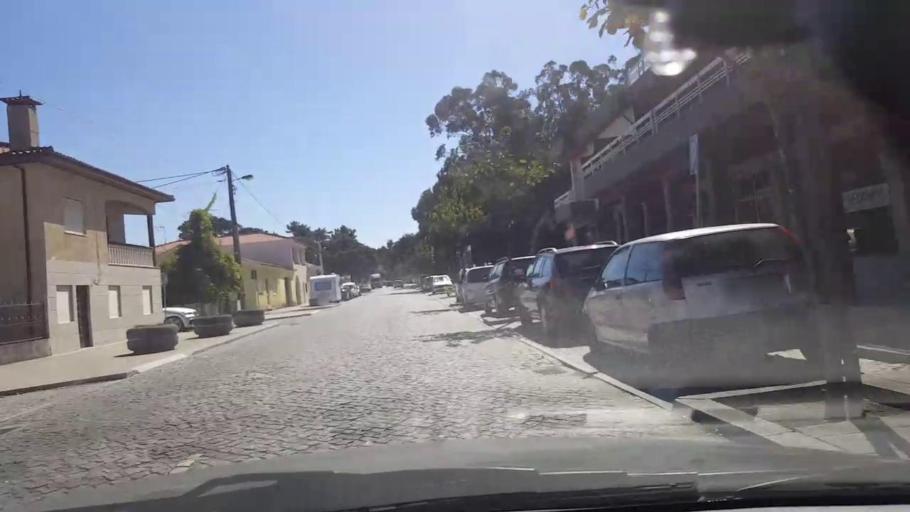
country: PT
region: Porto
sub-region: Vila do Conde
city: Arvore
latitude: 41.3325
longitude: -8.7309
